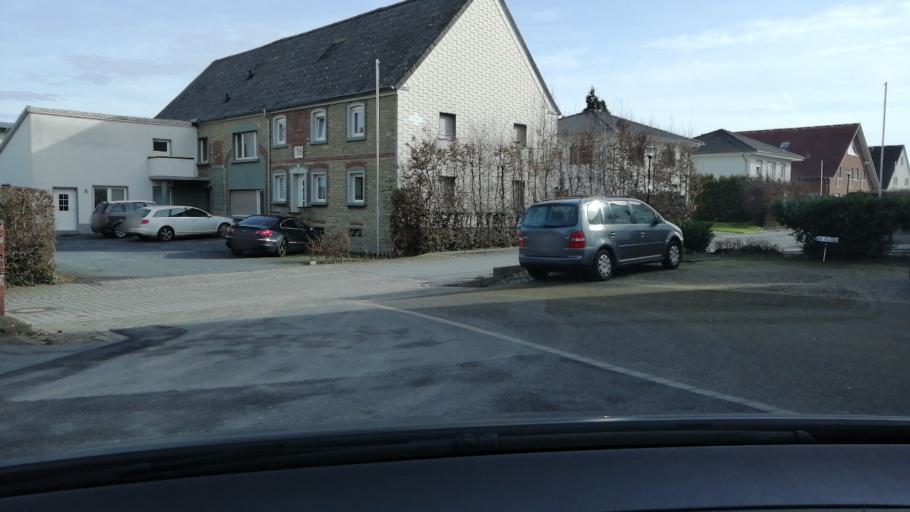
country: DE
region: North Rhine-Westphalia
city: Wickede
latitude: 51.5498
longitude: 7.8565
